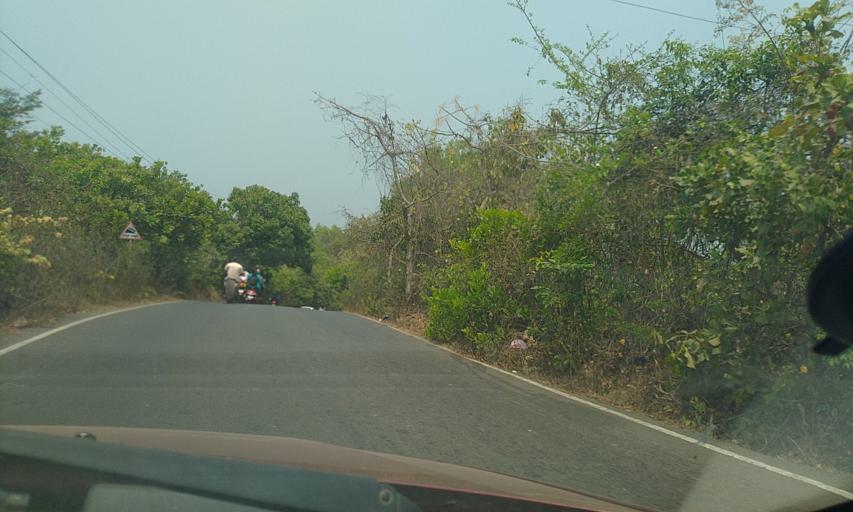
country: IN
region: Goa
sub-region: North Goa
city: Solim
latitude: 15.6136
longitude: 73.7929
